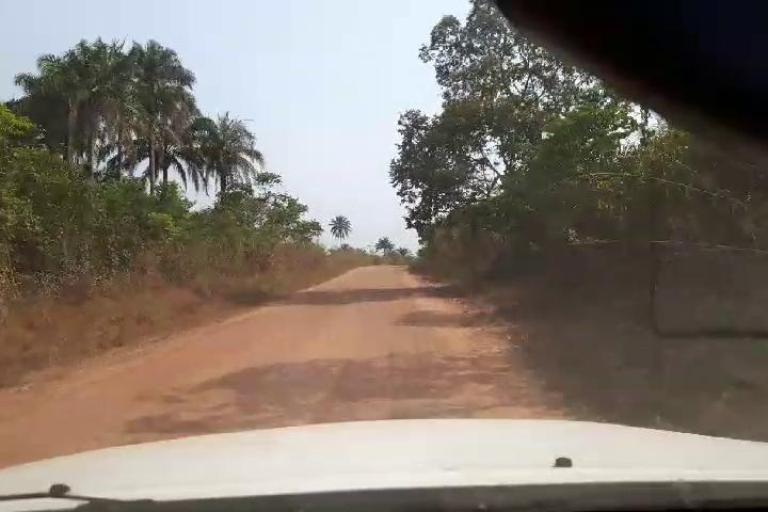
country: SL
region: Northern Province
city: Masingbi
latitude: 8.7943
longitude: -11.8685
